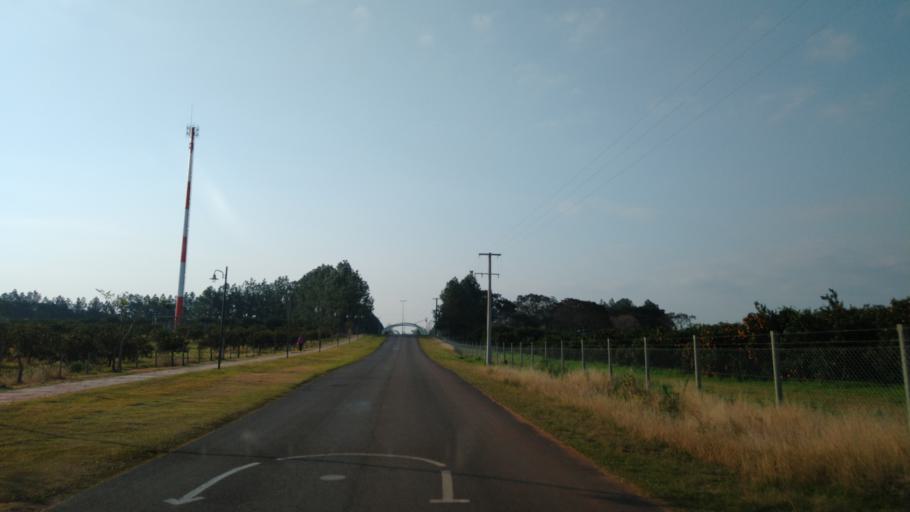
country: AR
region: Entre Rios
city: Santa Ana
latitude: -30.9023
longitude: -57.9247
